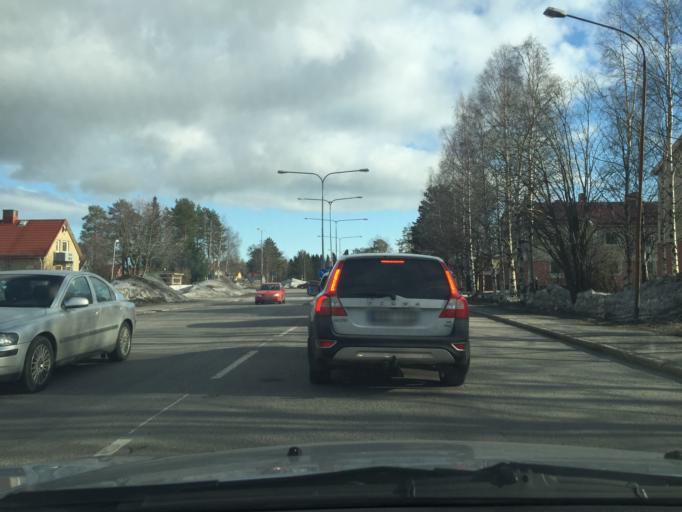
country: SE
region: Norrbotten
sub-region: Lulea Kommun
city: Lulea
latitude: 65.5840
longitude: 22.2070
